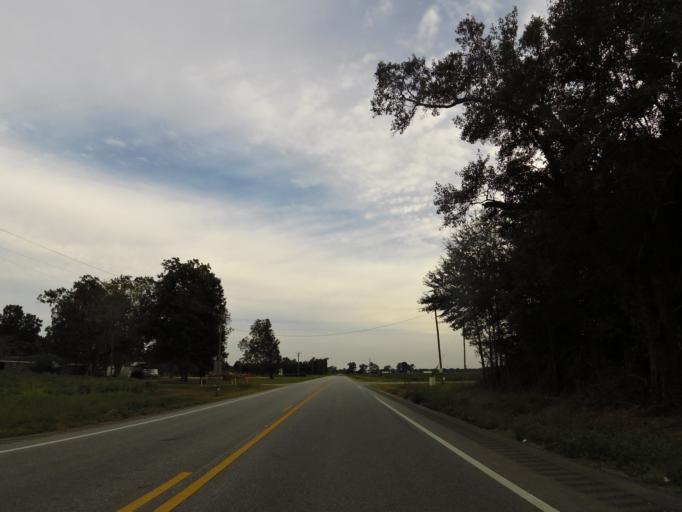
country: US
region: Alabama
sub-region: Monroe County
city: Frisco City
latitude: 31.3921
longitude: -87.4288
